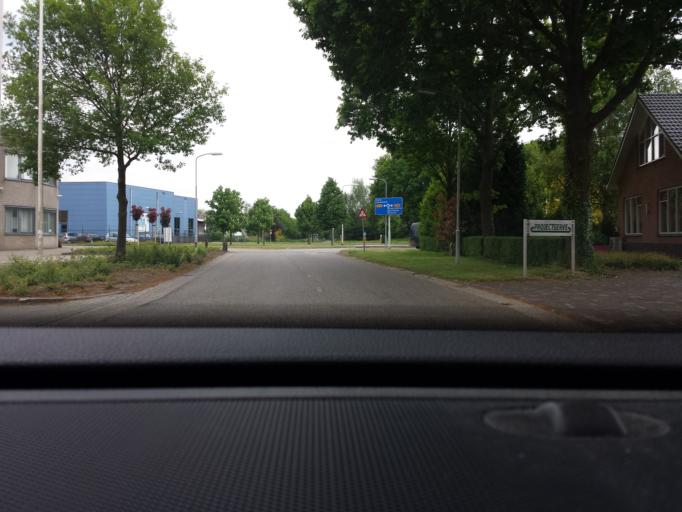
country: NL
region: Gelderland
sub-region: Gemeente Bronckhorst
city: Zelhem
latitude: 51.9993
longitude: 6.3537
